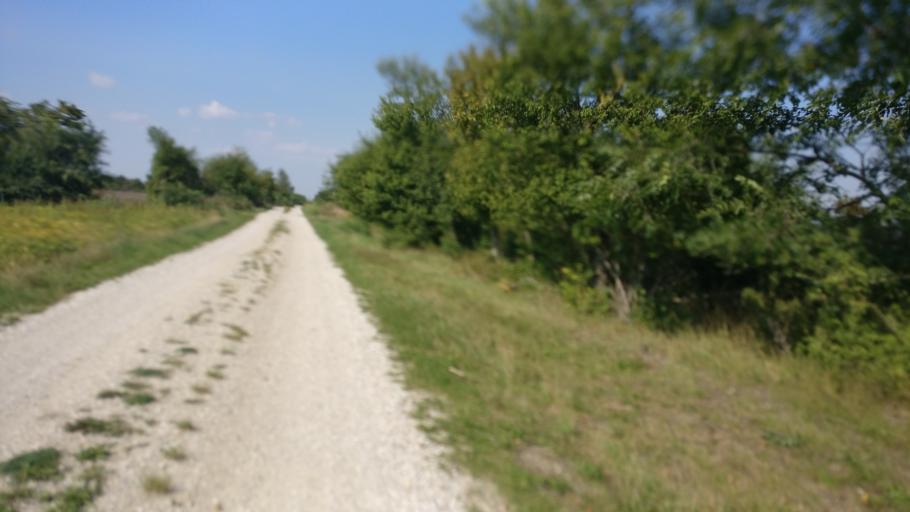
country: AT
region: Lower Austria
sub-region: Politischer Bezirk Modling
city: Munchendorf
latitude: 47.9984
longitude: 16.4005
